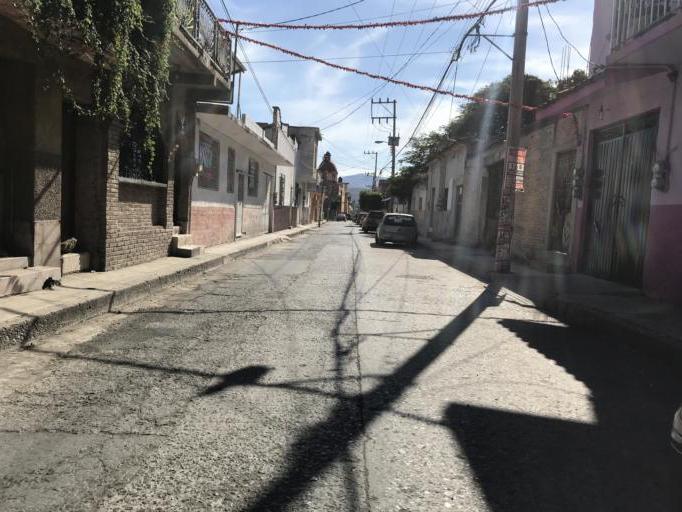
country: MX
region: Guerrero
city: Iguala de la Independencia
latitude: 18.3471
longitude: -99.5449
